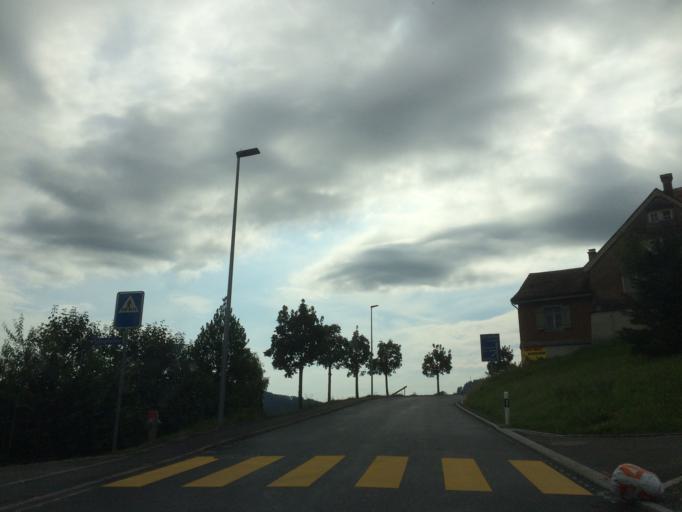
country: CH
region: Appenzell Ausserrhoden
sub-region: Bezirk Mittelland
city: Trogen
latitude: 47.4091
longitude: 9.4657
